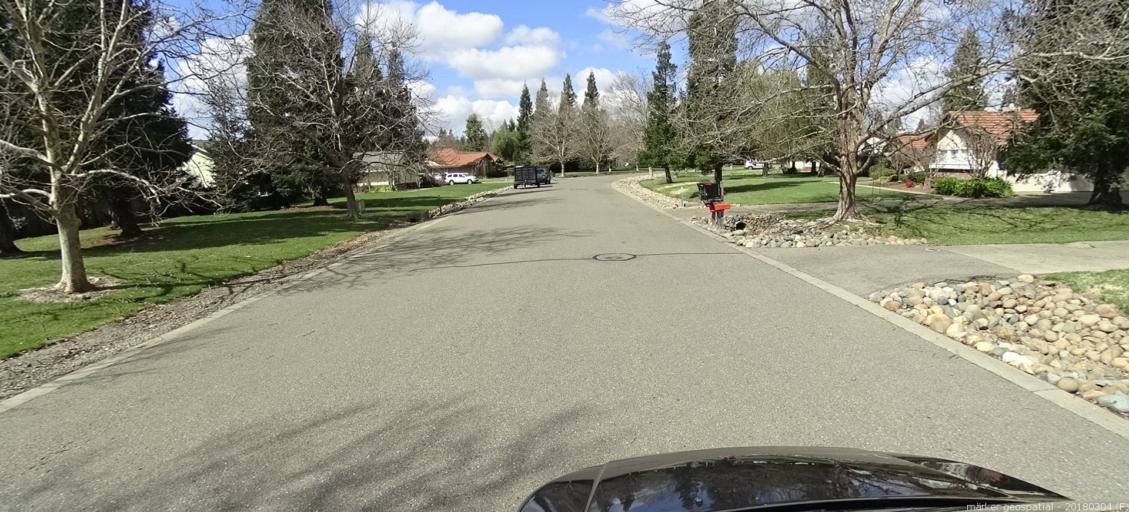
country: US
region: California
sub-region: Sacramento County
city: Vineyard
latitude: 38.4569
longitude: -121.3095
